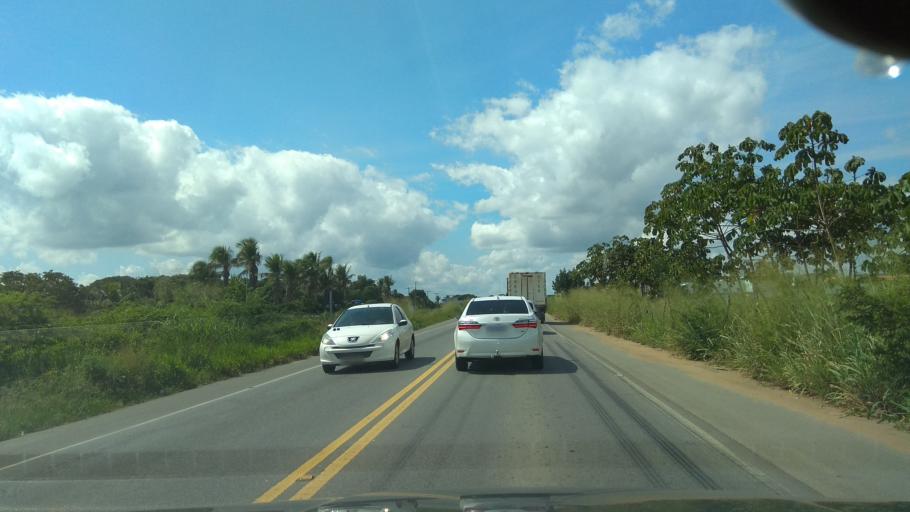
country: BR
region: Bahia
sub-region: Cruz Das Almas
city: Cruz das Almas
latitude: -12.6098
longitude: -39.0795
